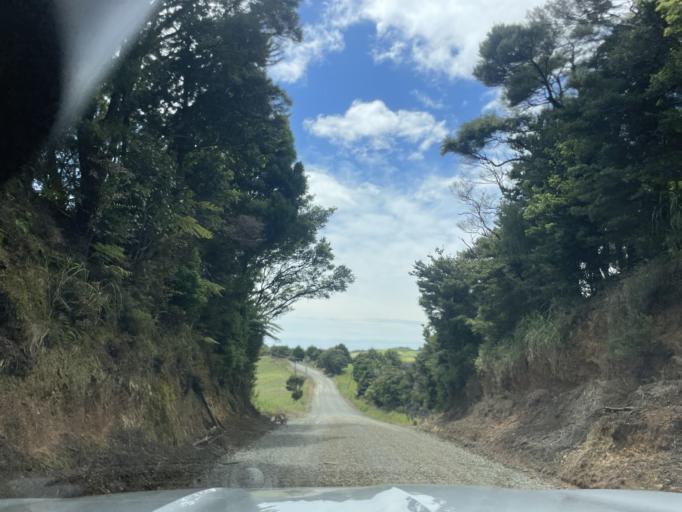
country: NZ
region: Auckland
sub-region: Auckland
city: Wellsford
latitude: -36.1615
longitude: 174.5327
